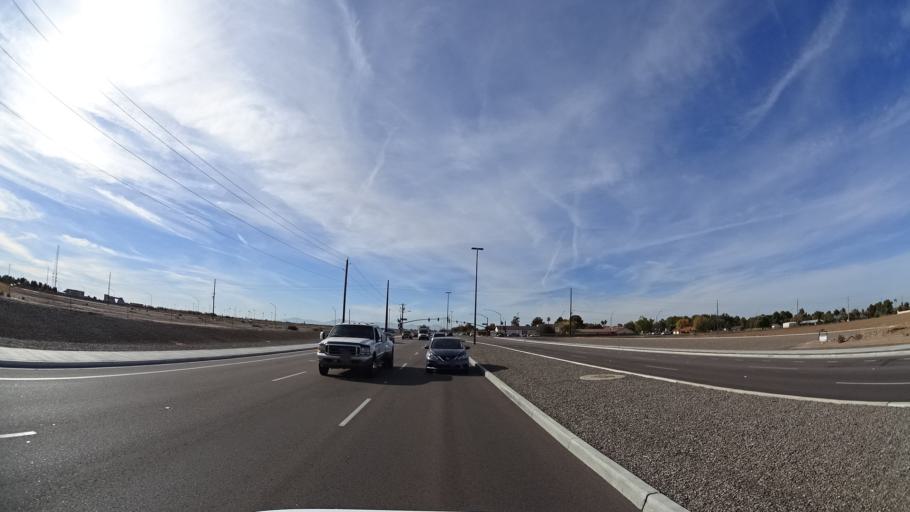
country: US
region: Arizona
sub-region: Maricopa County
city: Gilbert
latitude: 33.2774
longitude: -111.7362
